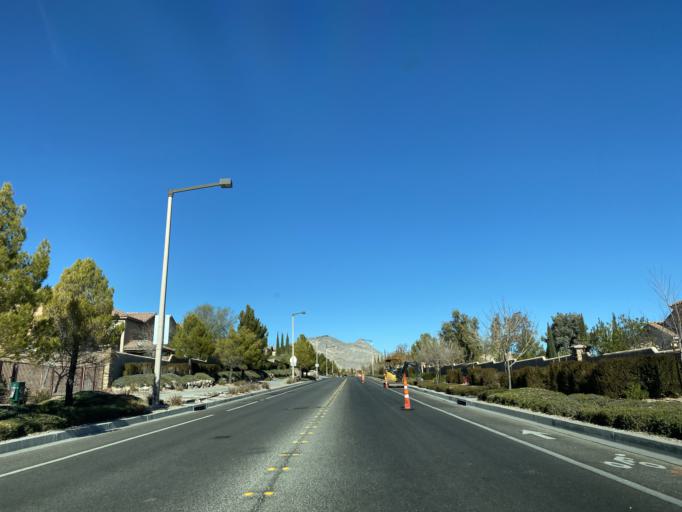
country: US
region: Nevada
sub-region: Clark County
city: Summerlin South
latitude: 36.1651
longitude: -115.3496
